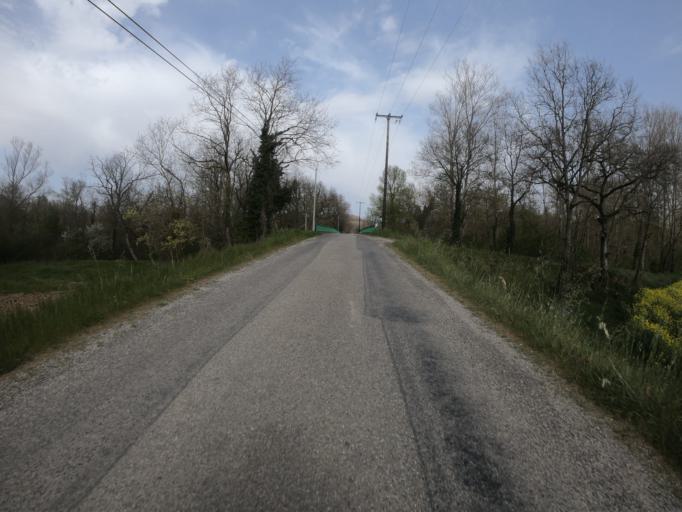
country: FR
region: Languedoc-Roussillon
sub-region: Departement de l'Aude
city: Belpech
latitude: 43.1720
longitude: 1.7307
